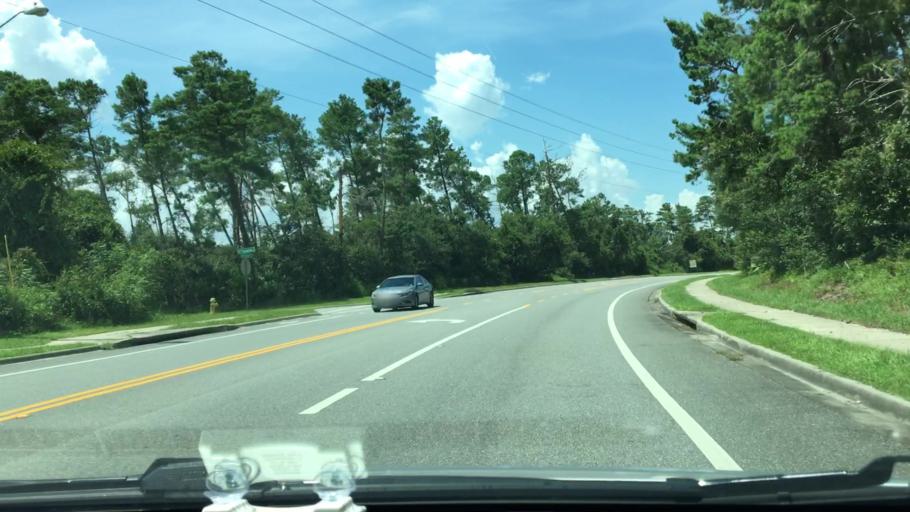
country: US
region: Florida
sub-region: Volusia County
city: Deltona
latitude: 28.8833
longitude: -81.2093
